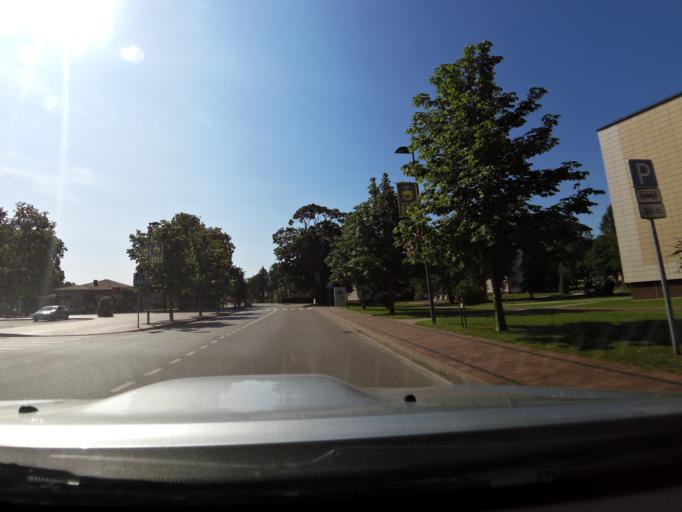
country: LT
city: Birstonas
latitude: 54.6053
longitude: 24.0284
